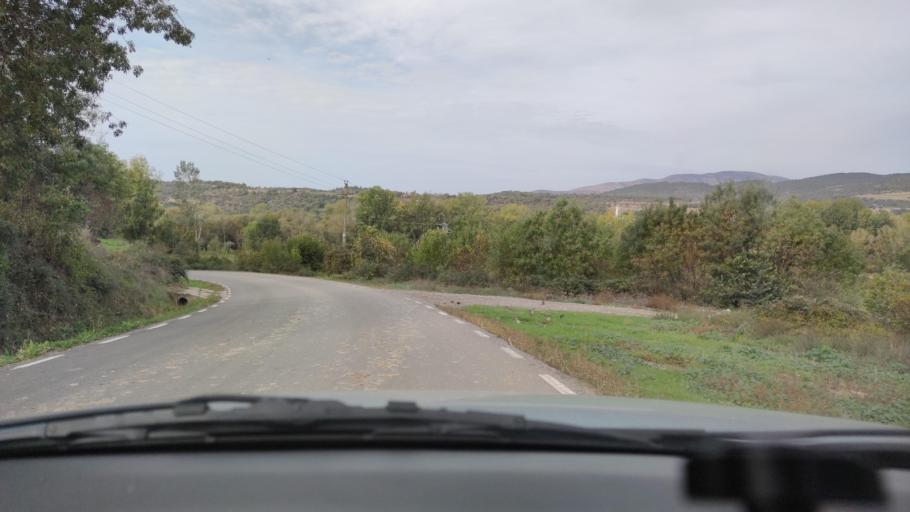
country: ES
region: Catalonia
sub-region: Provincia de Lleida
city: Artesa de Segre
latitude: 41.9184
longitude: 1.0828
